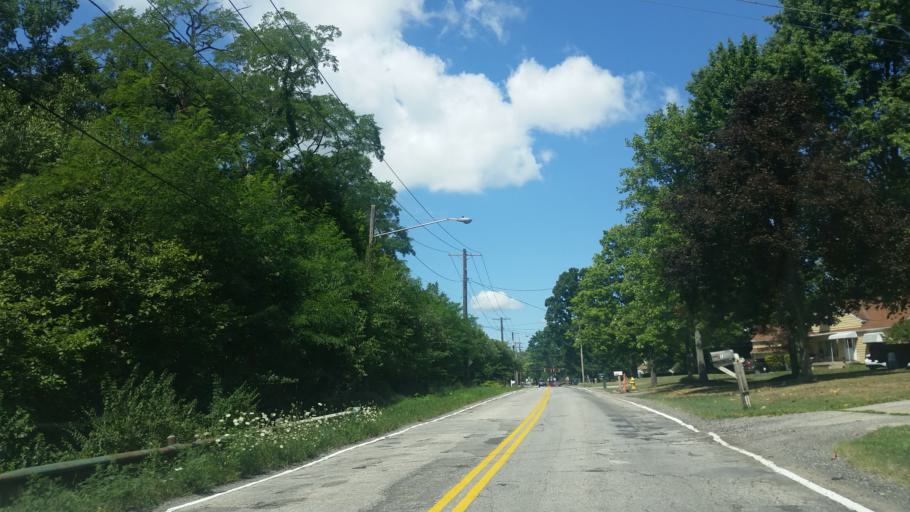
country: US
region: Ohio
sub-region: Cuyahoga County
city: Middleburg Heights
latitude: 41.3650
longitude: -81.7821
